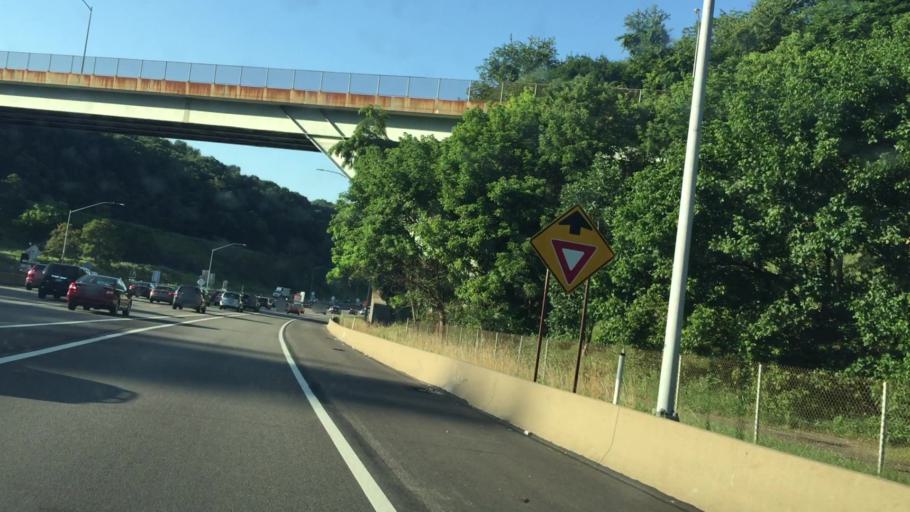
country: US
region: Pennsylvania
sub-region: Allegheny County
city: Millvale
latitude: 40.4838
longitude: -80.0082
